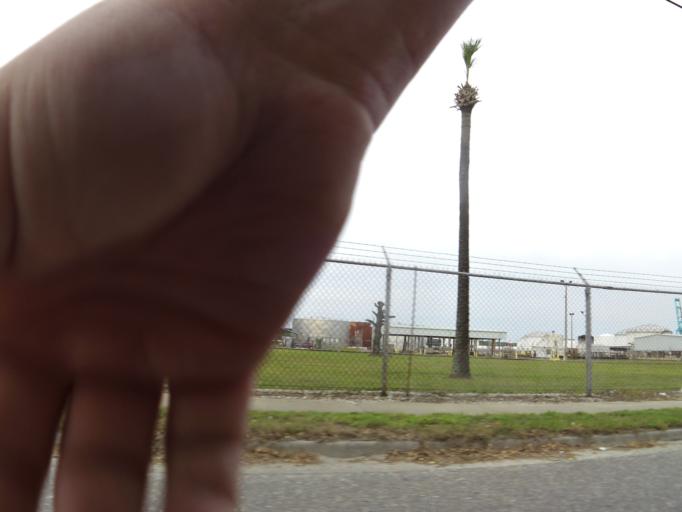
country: US
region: Florida
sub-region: Duval County
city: Jacksonville
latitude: 30.3602
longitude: -81.6269
